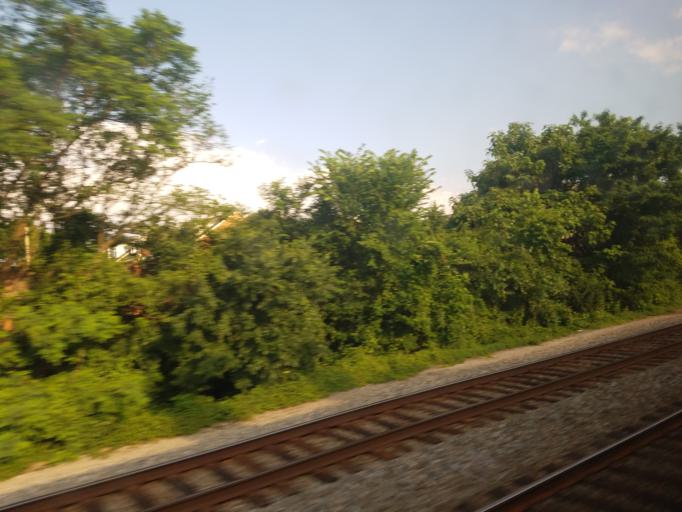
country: US
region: Virginia
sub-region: City of Alexandria
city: Alexandria
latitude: 38.8239
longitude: -77.0474
